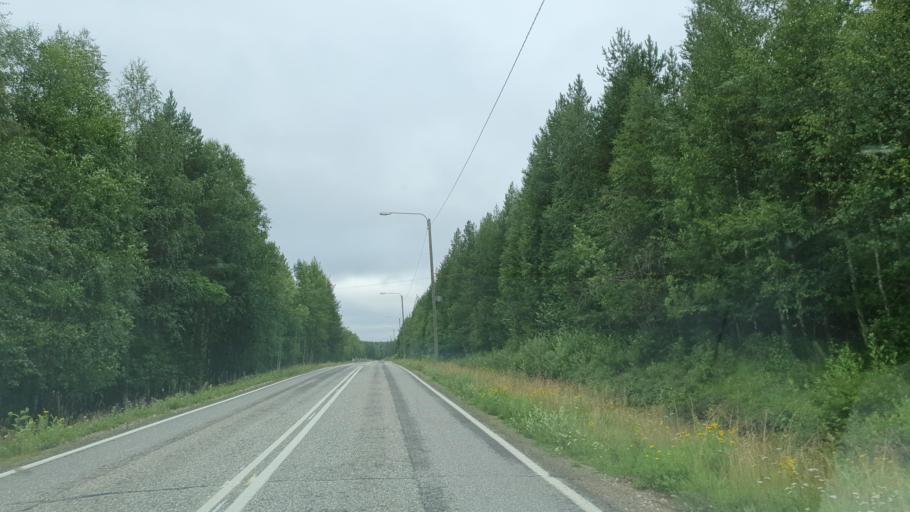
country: FI
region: Lapland
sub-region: Pohjois-Lappi
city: Sodankylae
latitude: 67.3738
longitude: 26.8824
